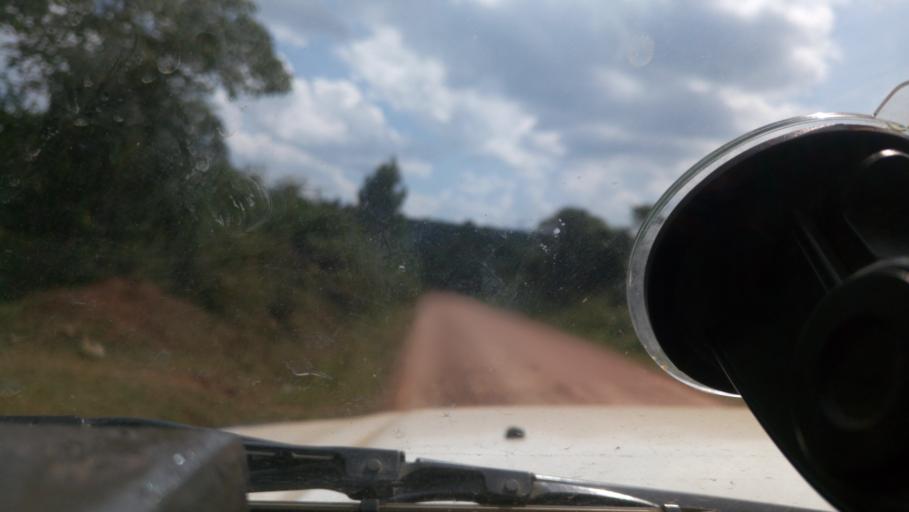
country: KE
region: Kericho
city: Sotik
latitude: -0.5946
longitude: 35.0695
